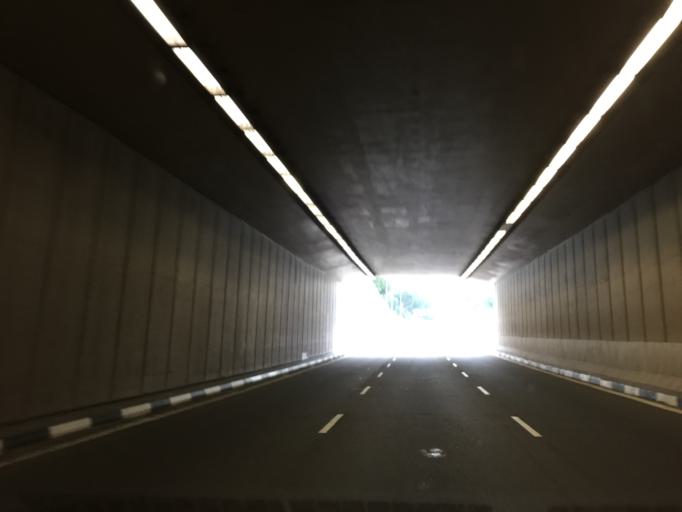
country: SG
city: Singapore
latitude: 1.3108
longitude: 103.8035
